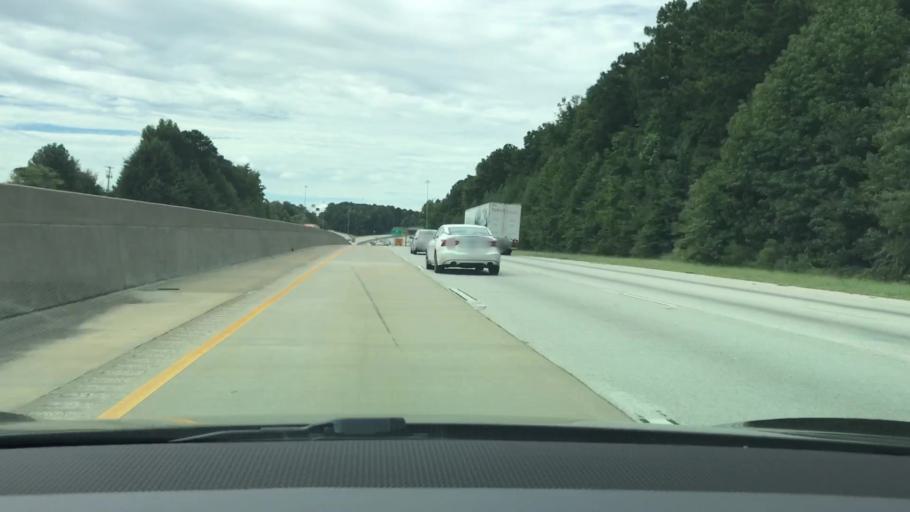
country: US
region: Georgia
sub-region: Fulton County
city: Palmetto
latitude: 33.4487
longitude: -84.6855
